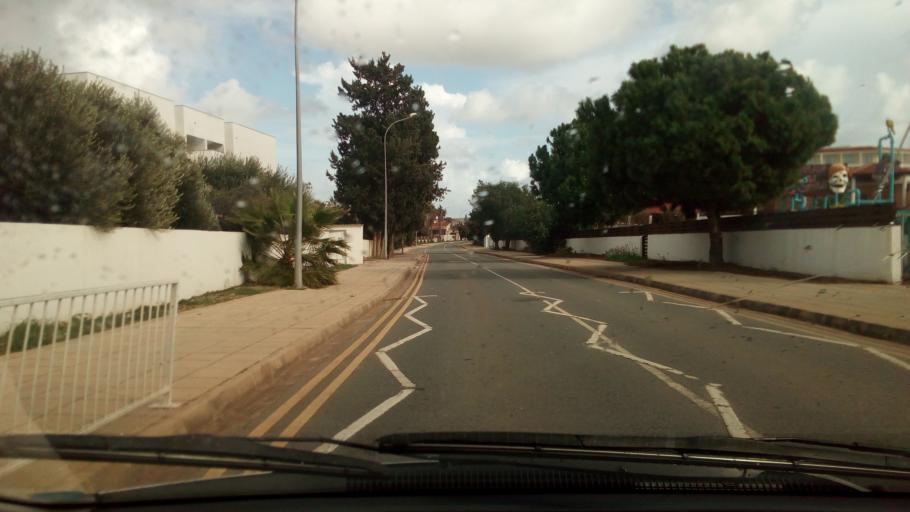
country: CY
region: Ammochostos
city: Ayia Napa
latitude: 34.9908
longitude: 33.9668
